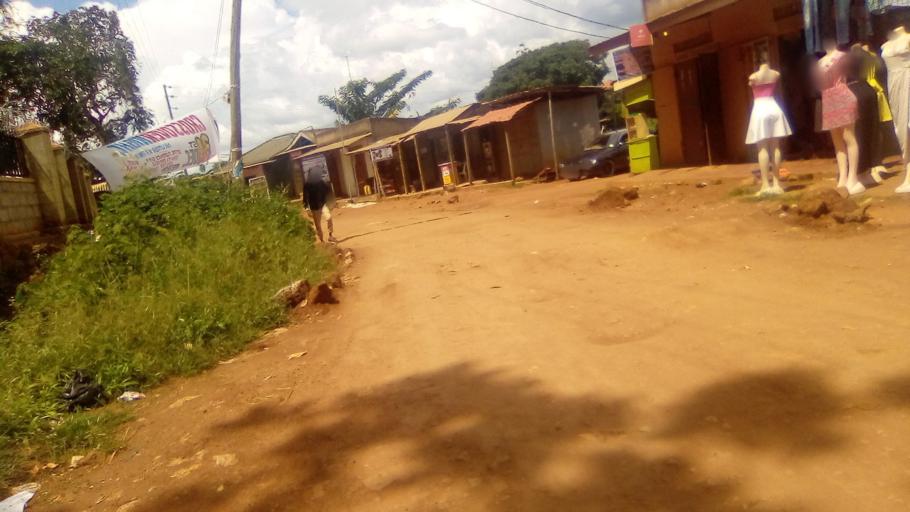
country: UG
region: Central Region
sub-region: Wakiso District
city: Entebbe
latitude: 0.0966
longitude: 32.5068
